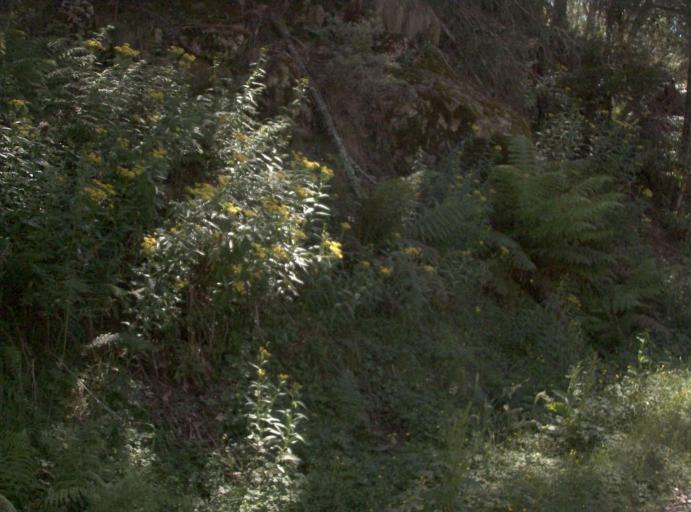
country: AU
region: Victoria
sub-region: Yarra Ranges
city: Millgrove
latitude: -37.7084
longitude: 145.6793
